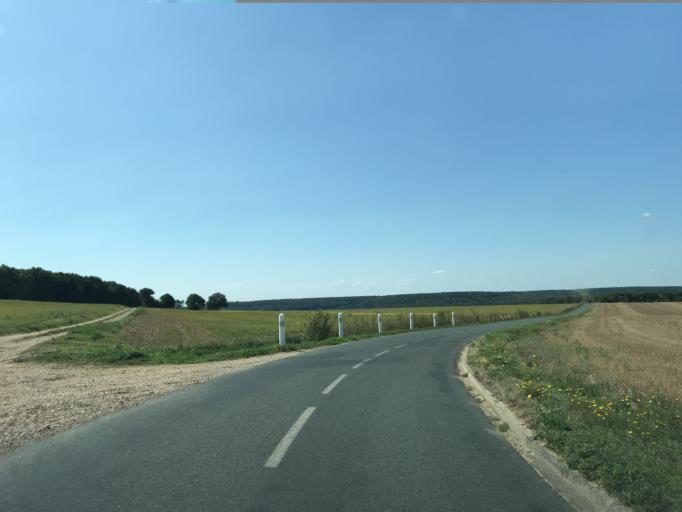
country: FR
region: Haute-Normandie
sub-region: Departement de l'Eure
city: Houlbec-Cocherel
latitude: 49.0829
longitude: 1.3205
